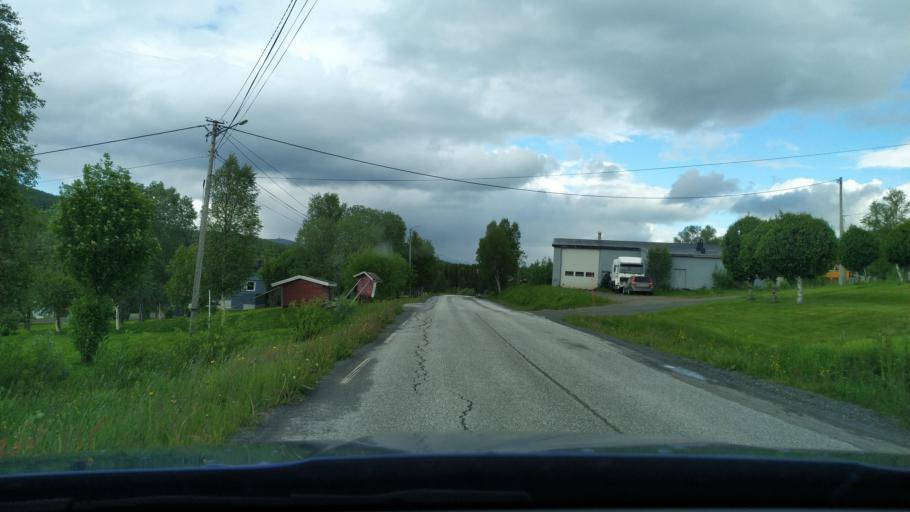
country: NO
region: Troms
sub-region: Dyroy
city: Brostadbotn
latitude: 69.0840
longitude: 17.6902
